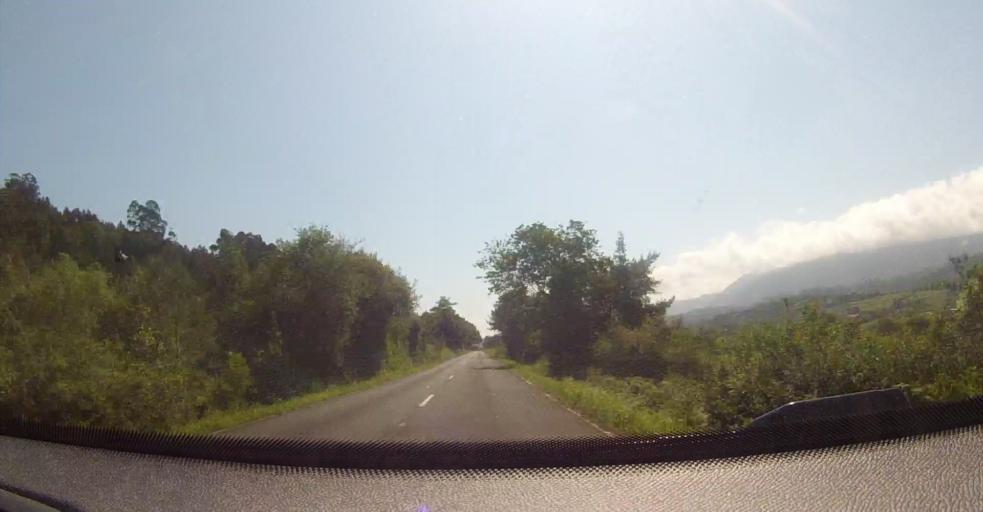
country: ES
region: Asturias
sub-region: Province of Asturias
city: Colunga
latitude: 43.4883
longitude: -5.3006
